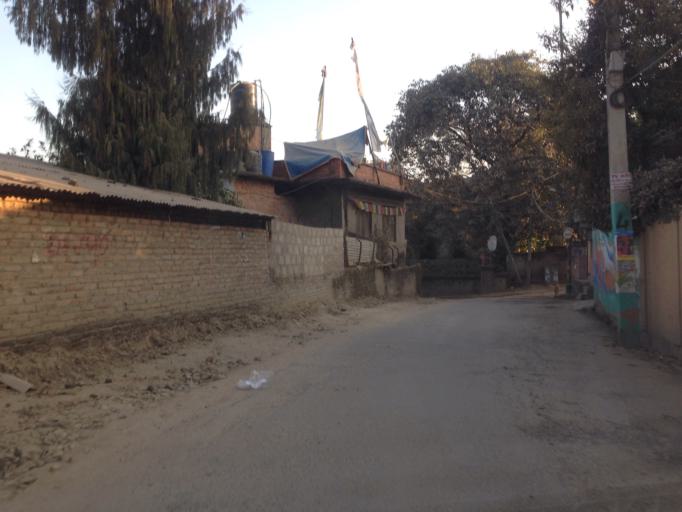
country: NP
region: Central Region
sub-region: Bagmati Zone
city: Kathmandu
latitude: 27.7131
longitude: 85.3001
